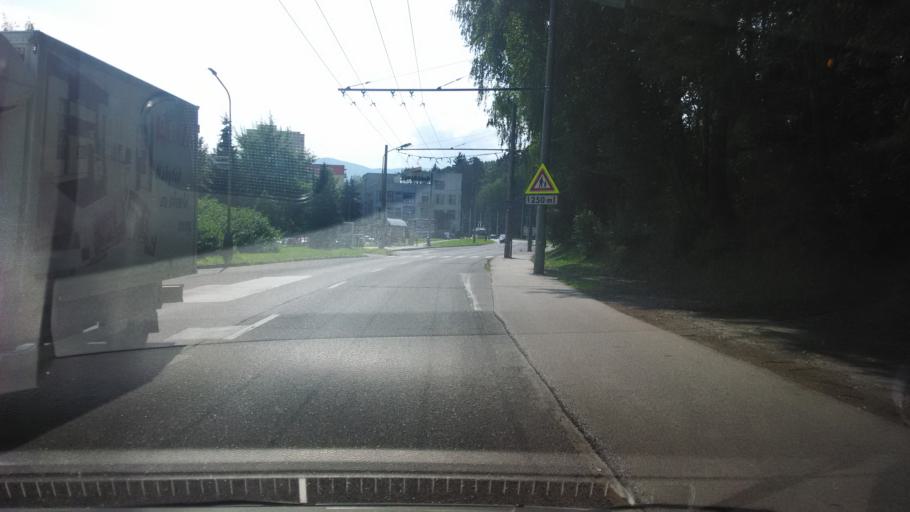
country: SK
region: Zilinsky
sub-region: Okres Zilina
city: Zilina
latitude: 49.2059
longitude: 18.7626
